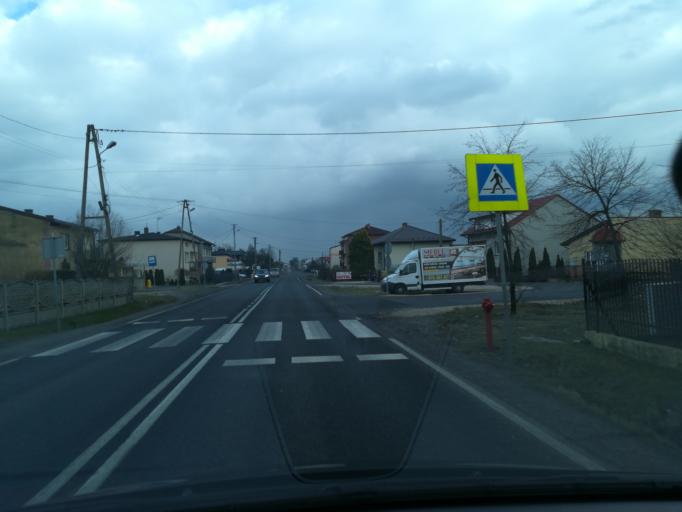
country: PL
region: Lodz Voivodeship
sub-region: Powiat radomszczanski
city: Radomsko
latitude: 51.0783
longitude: 19.3862
